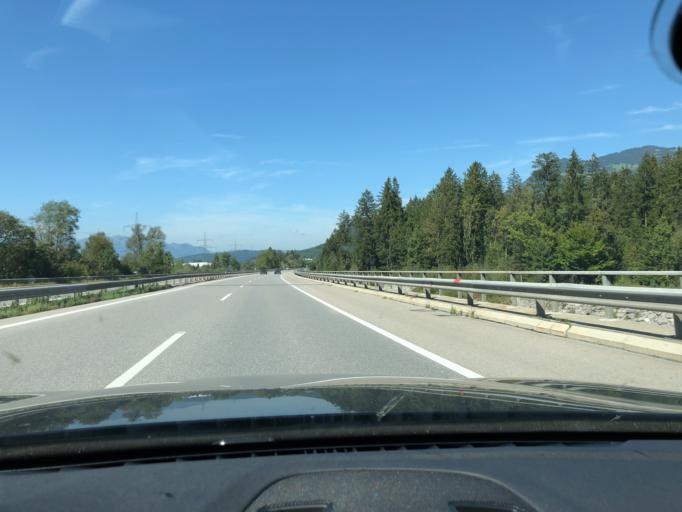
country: AT
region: Vorarlberg
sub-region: Politischer Bezirk Bludenz
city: Bludesch
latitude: 47.1804
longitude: 9.7289
